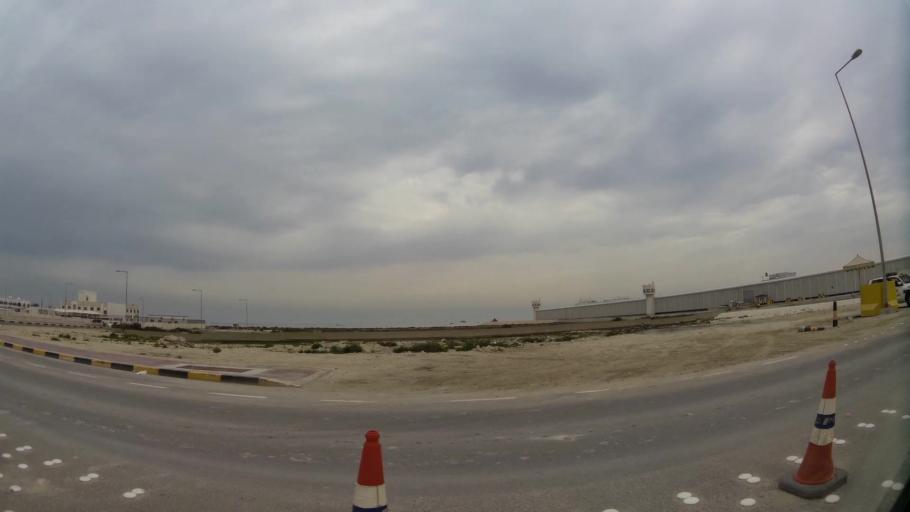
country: BH
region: Central Governorate
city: Dar Kulayb
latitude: 25.9954
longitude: 50.6163
